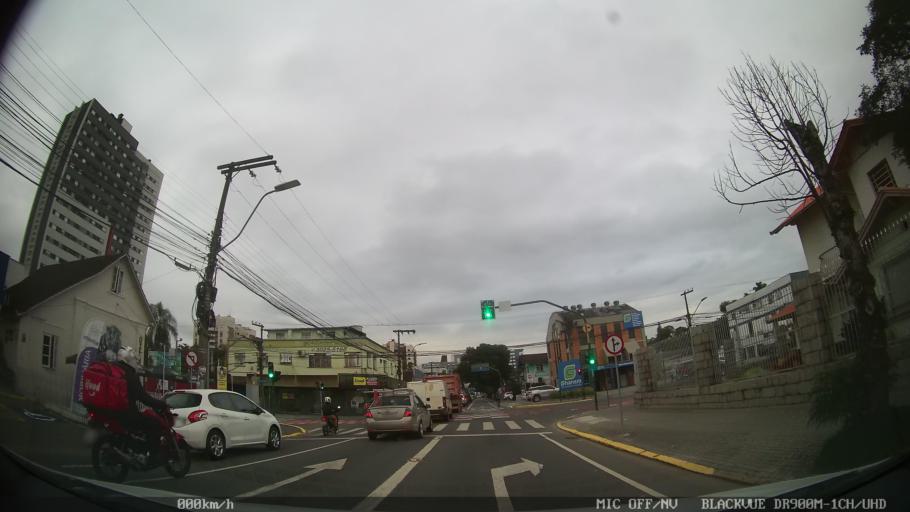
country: BR
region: Santa Catarina
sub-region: Joinville
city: Joinville
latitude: -26.2945
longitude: -48.8502
